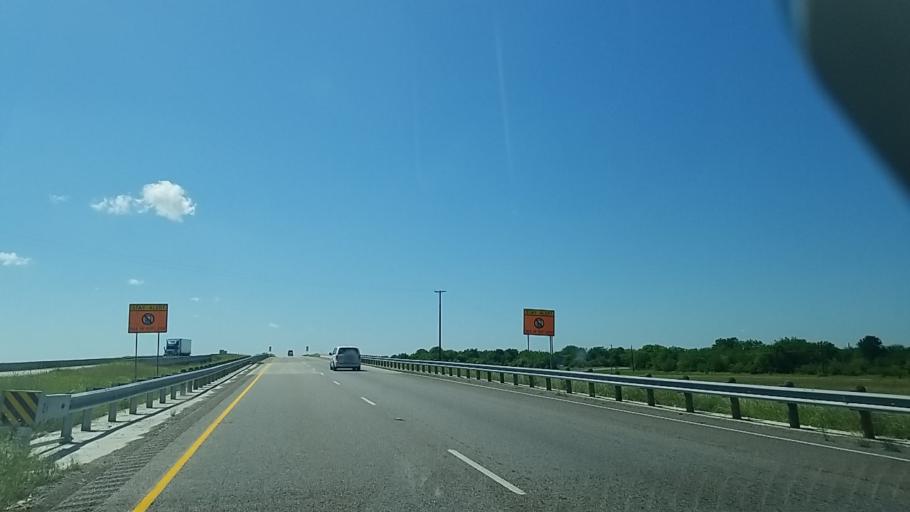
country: US
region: Texas
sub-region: Freestone County
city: Wortham
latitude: 31.8637
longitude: -96.3186
